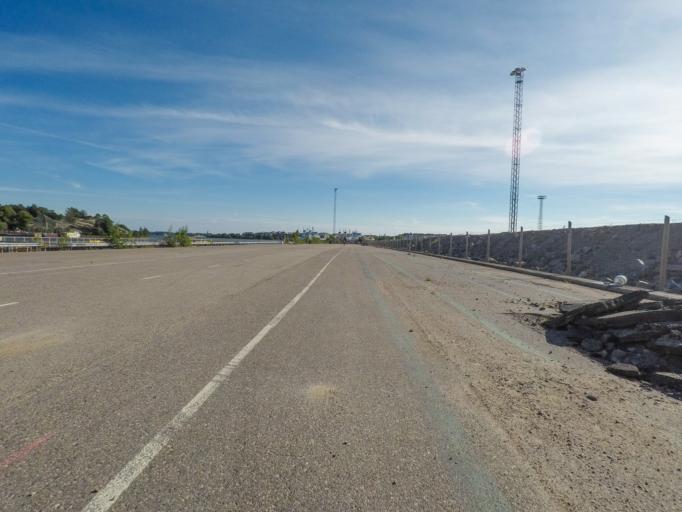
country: FI
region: Uusimaa
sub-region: Helsinki
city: Helsinki
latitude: 60.1778
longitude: 24.9765
